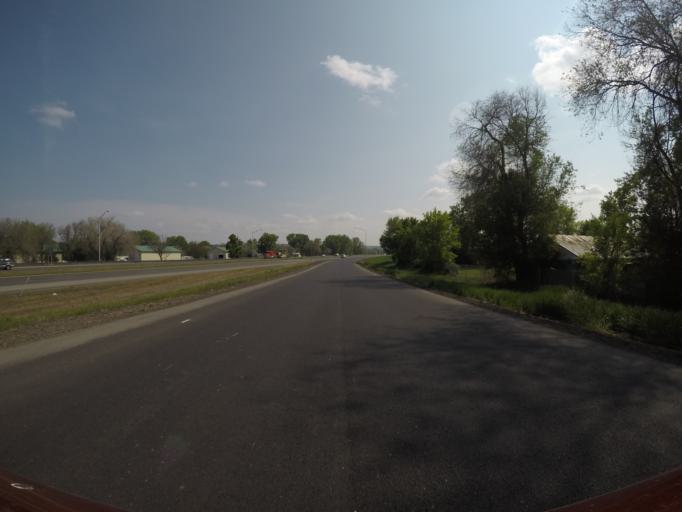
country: US
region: Montana
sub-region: Yellowstone County
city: Billings
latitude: 45.7658
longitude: -108.4883
